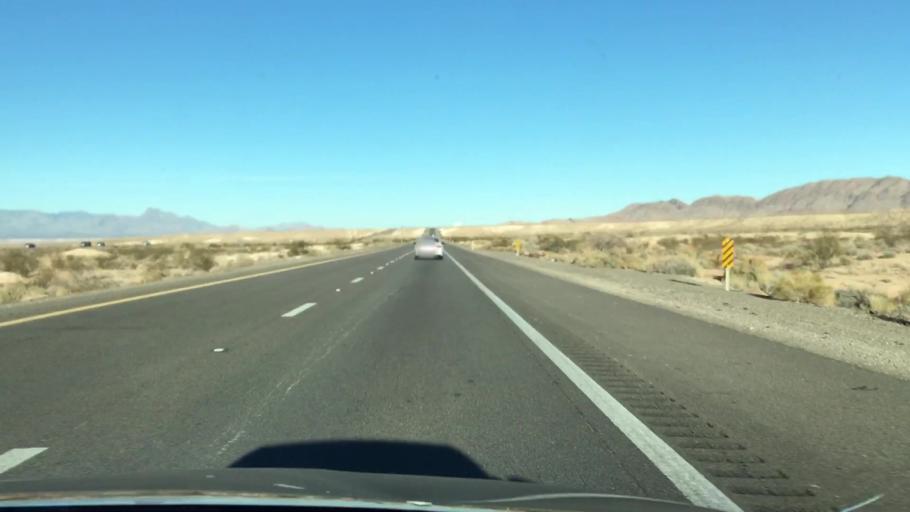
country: US
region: Nevada
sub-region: Clark County
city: Moapa Town
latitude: 36.5590
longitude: -114.6864
